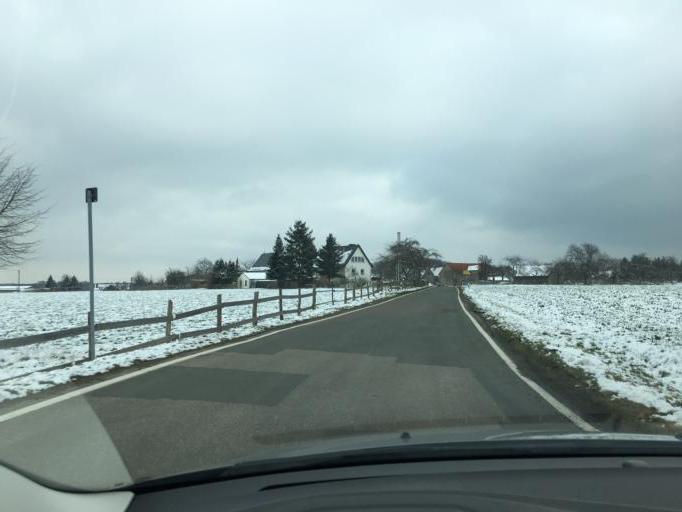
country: DE
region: Saxony
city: Bad Lausick
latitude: 51.1386
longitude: 12.6844
